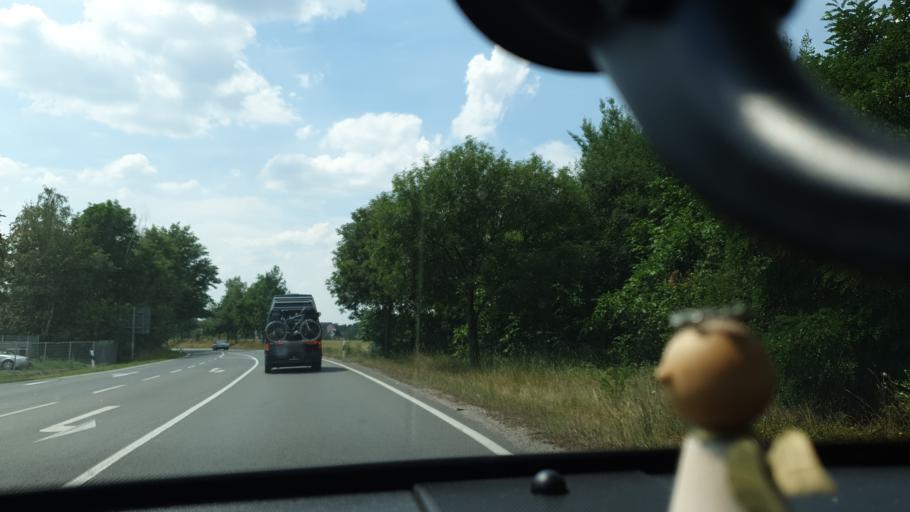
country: DE
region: Saxony
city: Taucha
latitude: 51.3891
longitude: 12.5046
